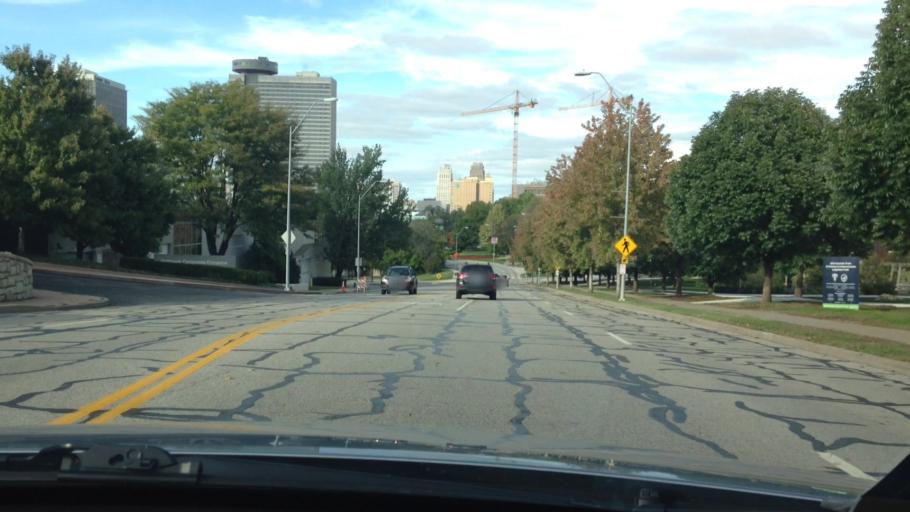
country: US
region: Missouri
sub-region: Jackson County
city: Kansas City
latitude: 39.0798
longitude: -94.5784
